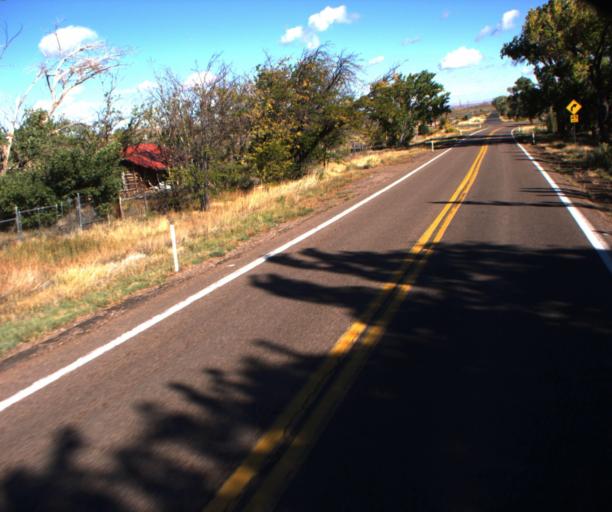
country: US
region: Arizona
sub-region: Apache County
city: Saint Johns
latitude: 34.4642
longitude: -109.6183
